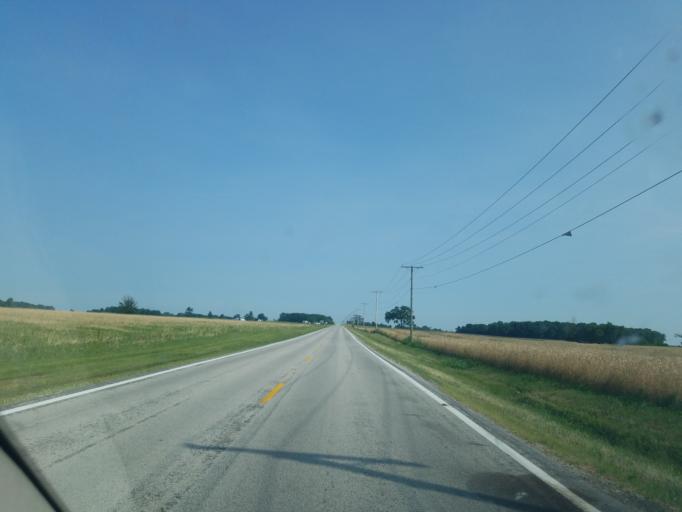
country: US
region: Ohio
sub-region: Wyandot County
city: Carey
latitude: 41.0238
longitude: -83.2937
